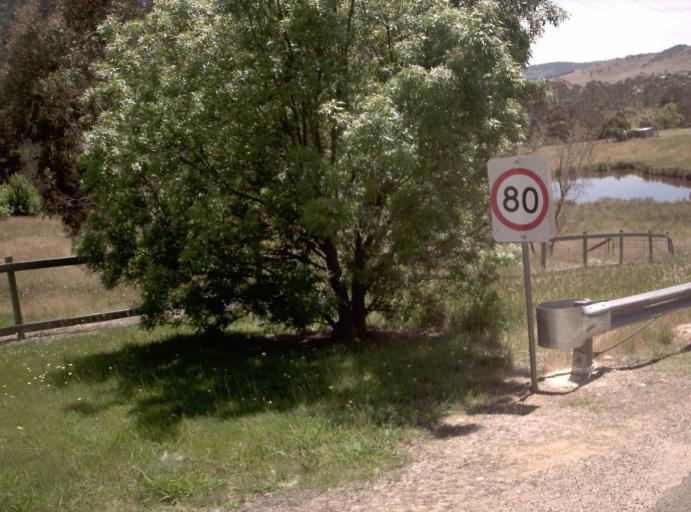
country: AU
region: Victoria
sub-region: Alpine
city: Mount Beauty
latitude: -37.1035
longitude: 147.5829
